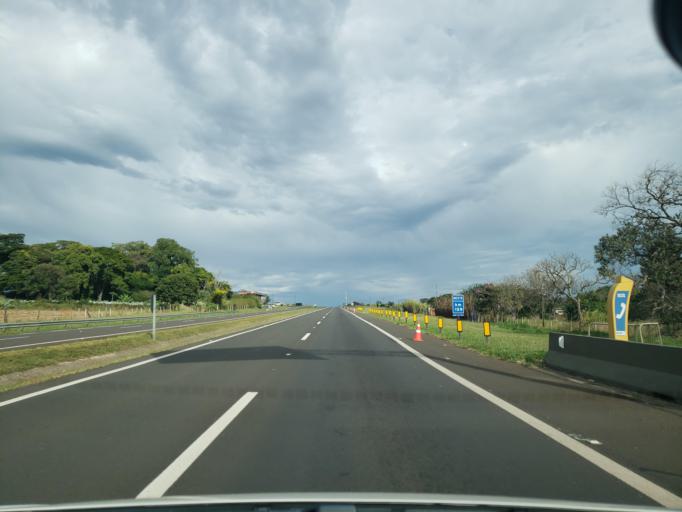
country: BR
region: Sao Paulo
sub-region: Dois Corregos
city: Dois Corregos
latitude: -22.2608
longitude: -48.3730
